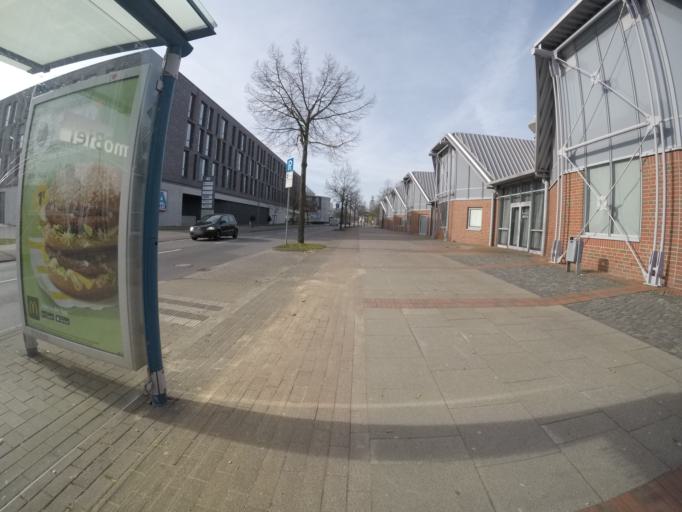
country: DE
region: North Rhine-Westphalia
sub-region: Regierungsbezirk Detmold
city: Bielefeld
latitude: 52.0254
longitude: 8.5517
